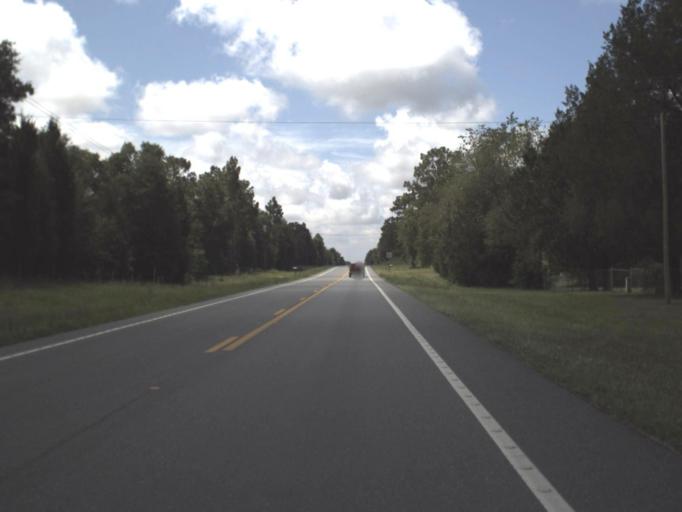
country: US
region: Florida
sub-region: Gilchrist County
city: Trenton
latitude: 29.8064
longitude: -82.8670
